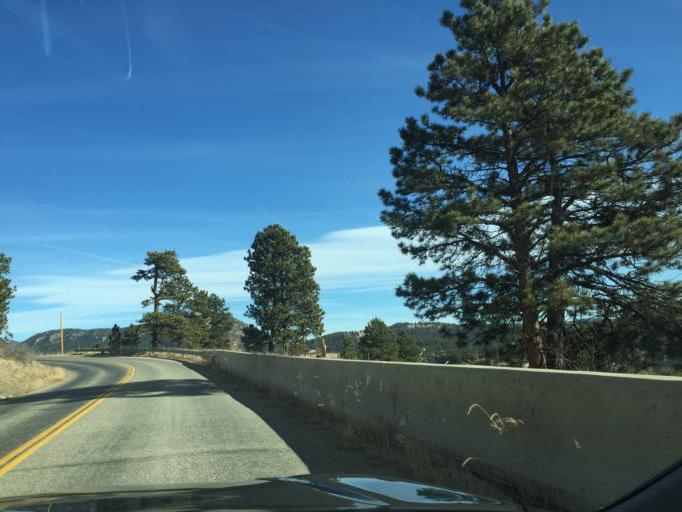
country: US
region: Colorado
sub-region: Jefferson County
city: Evergreen
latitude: 39.4378
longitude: -105.4577
